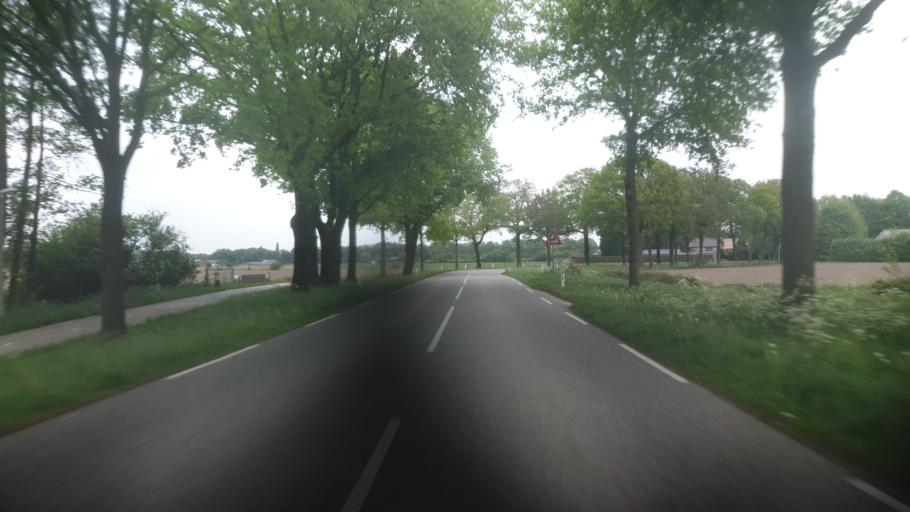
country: NL
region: North Brabant
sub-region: Gemeente Grave
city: Grave
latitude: 51.7747
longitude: 5.7898
